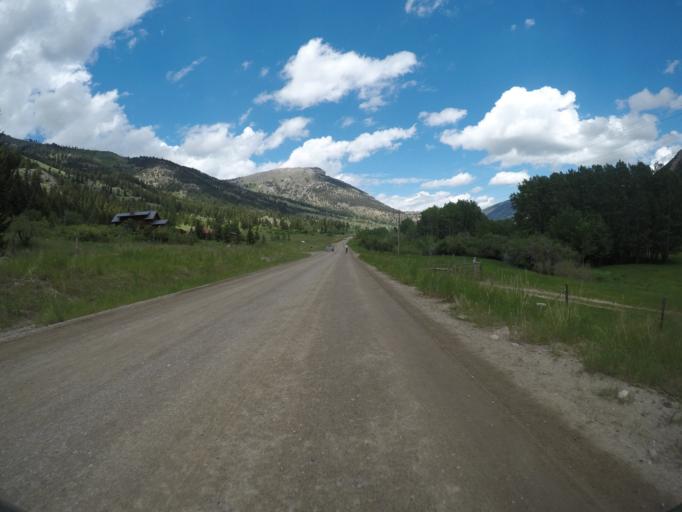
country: US
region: Montana
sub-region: Park County
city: Livingston
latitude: 45.5150
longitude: -110.2266
